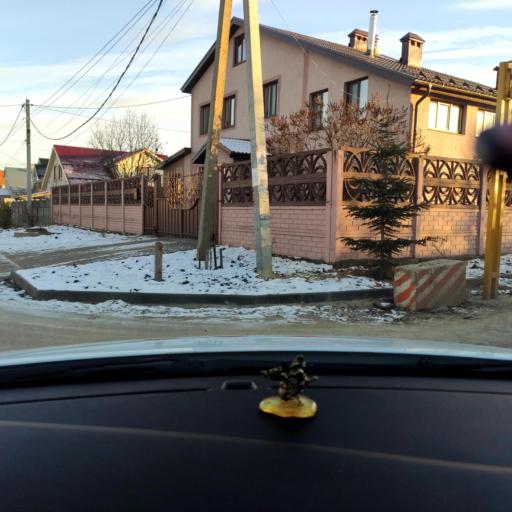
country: RU
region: Tatarstan
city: Stolbishchi
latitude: 55.6064
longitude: 49.1413
